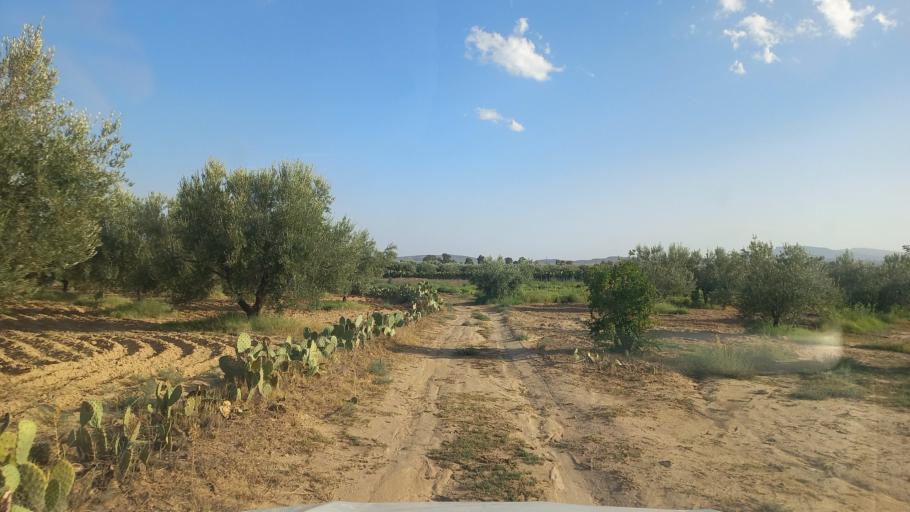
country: TN
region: Al Qasrayn
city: Kasserine
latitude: 35.2664
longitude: 9.0328
